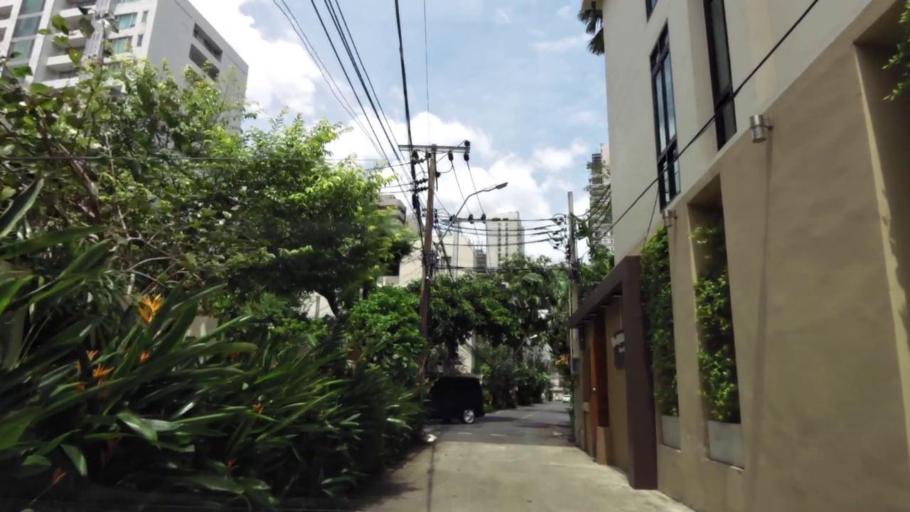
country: TH
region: Bangkok
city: Khlong Toei
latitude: 13.7272
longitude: 100.5662
